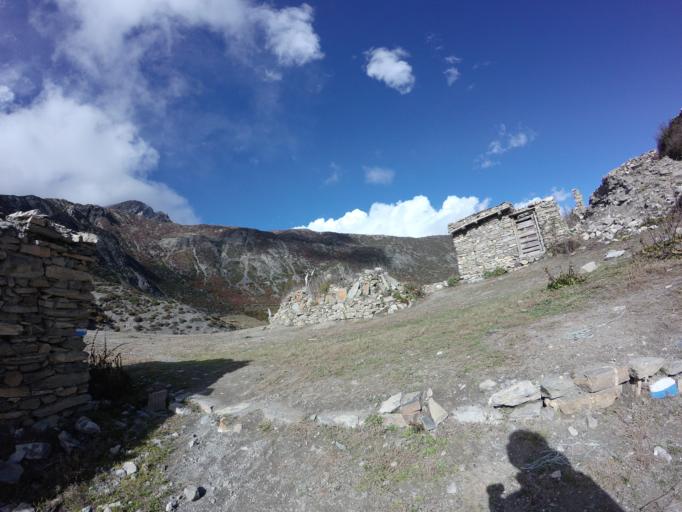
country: NP
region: Western Region
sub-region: Gandaki Zone
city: Nawal
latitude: 28.6770
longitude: 83.9721
